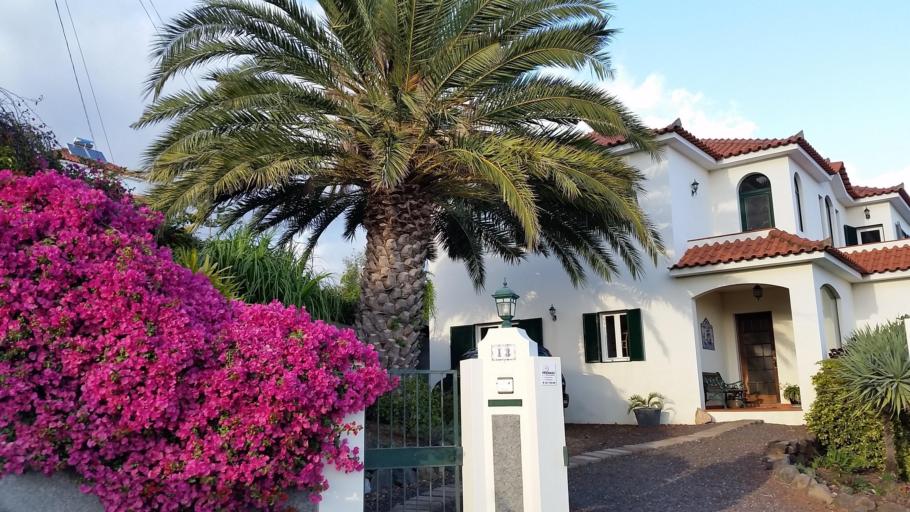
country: PT
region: Madeira
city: Canico
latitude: 32.6457
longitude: -16.8353
